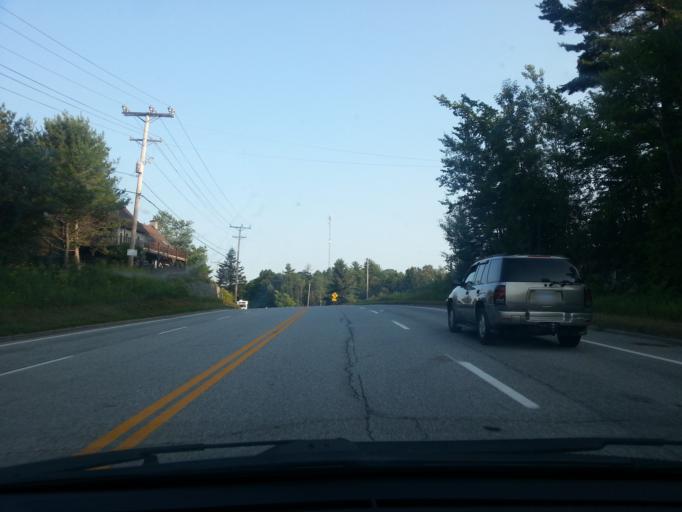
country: CA
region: Quebec
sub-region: Outaouais
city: Wakefield
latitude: 45.8228
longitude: -75.9560
